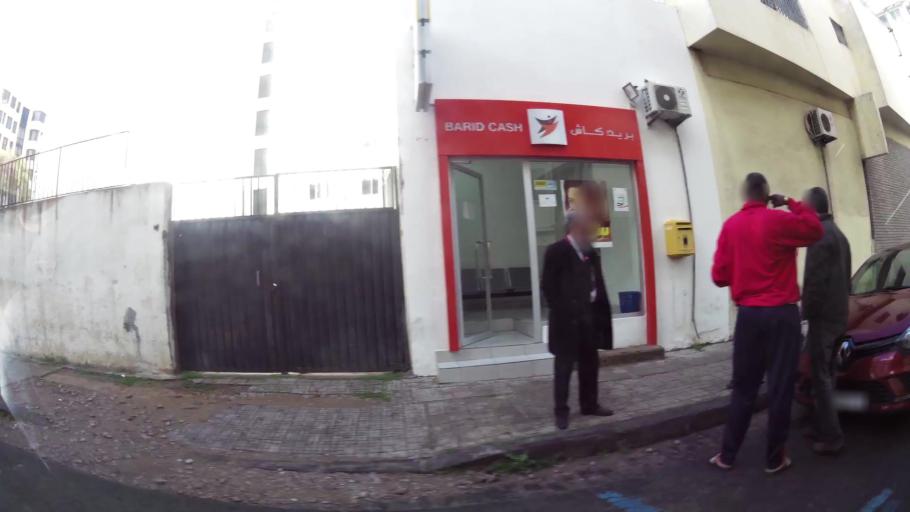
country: MA
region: Grand Casablanca
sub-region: Casablanca
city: Casablanca
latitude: 33.5836
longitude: -7.6142
